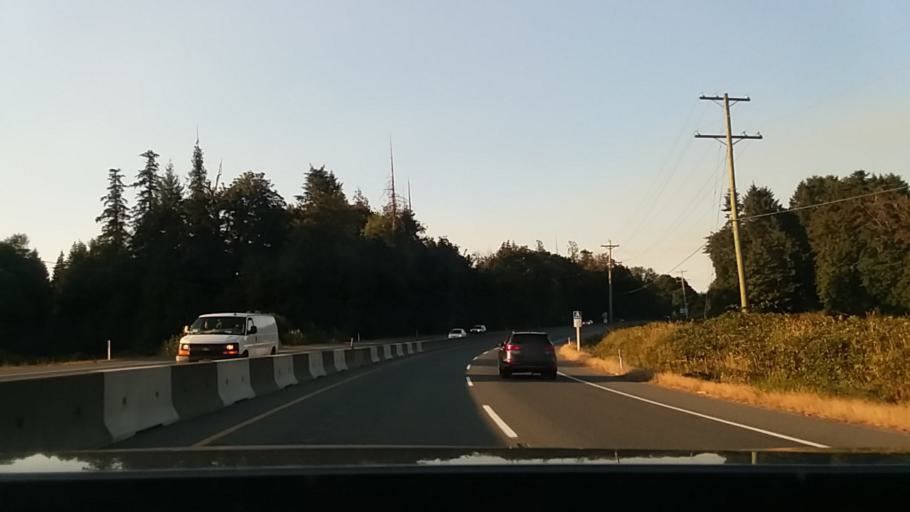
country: CA
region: British Columbia
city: North Cowichan
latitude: 48.8700
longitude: -123.7110
